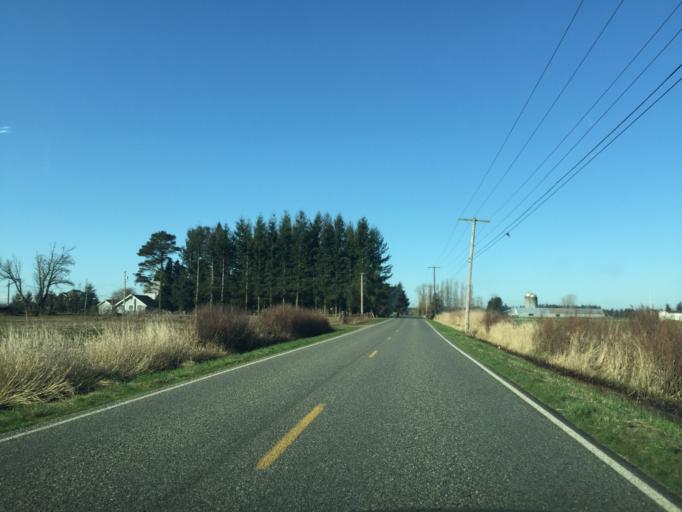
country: US
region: Washington
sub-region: Whatcom County
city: Marietta-Alderwood
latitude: 48.8552
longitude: -122.5044
